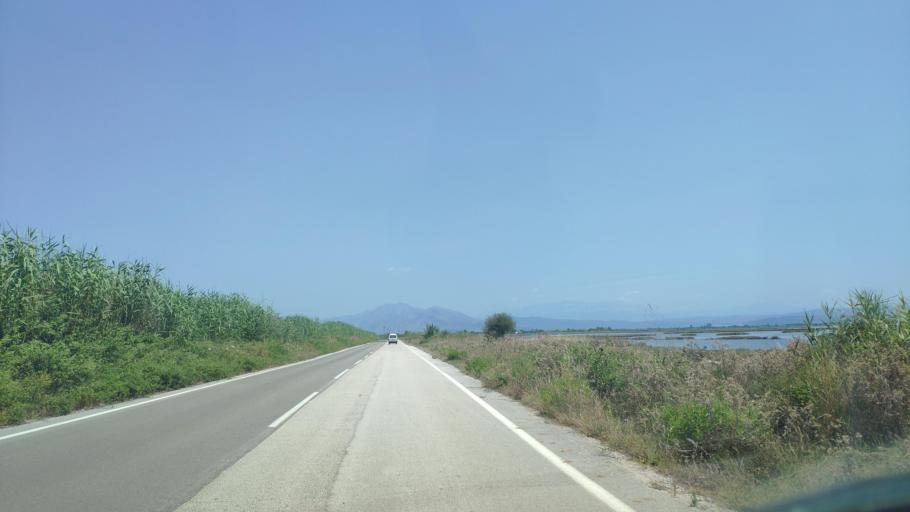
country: GR
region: Epirus
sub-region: Nomos Artas
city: Aneza
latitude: 39.0457
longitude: 20.8609
